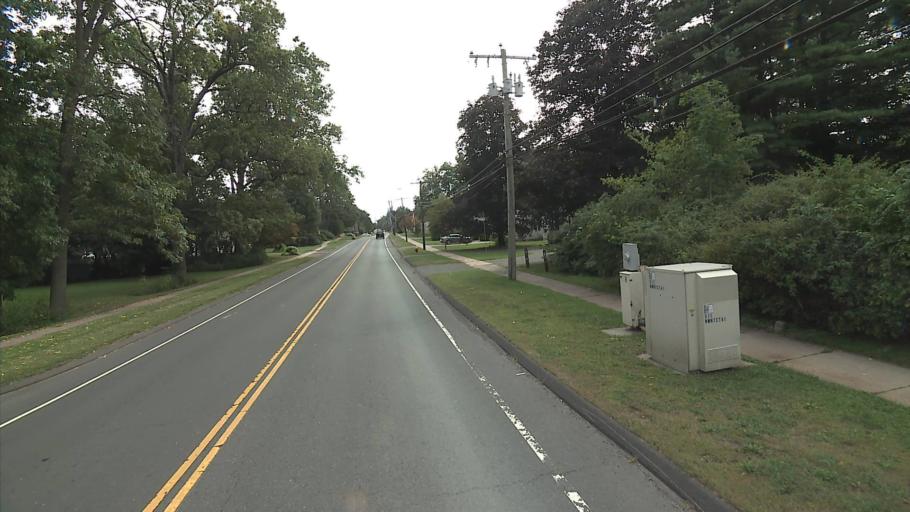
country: US
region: Connecticut
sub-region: Hartford County
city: Newington
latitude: 41.7044
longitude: -72.7253
